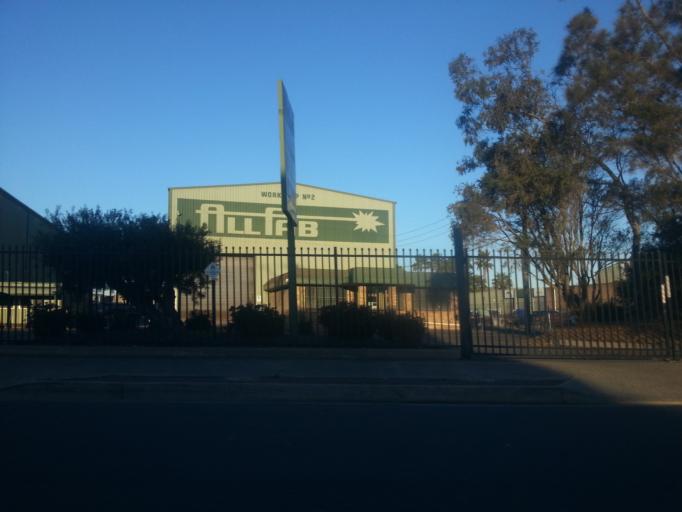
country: AU
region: New South Wales
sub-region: Wollongong
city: Port Kembla
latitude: -34.4930
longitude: 150.8931
